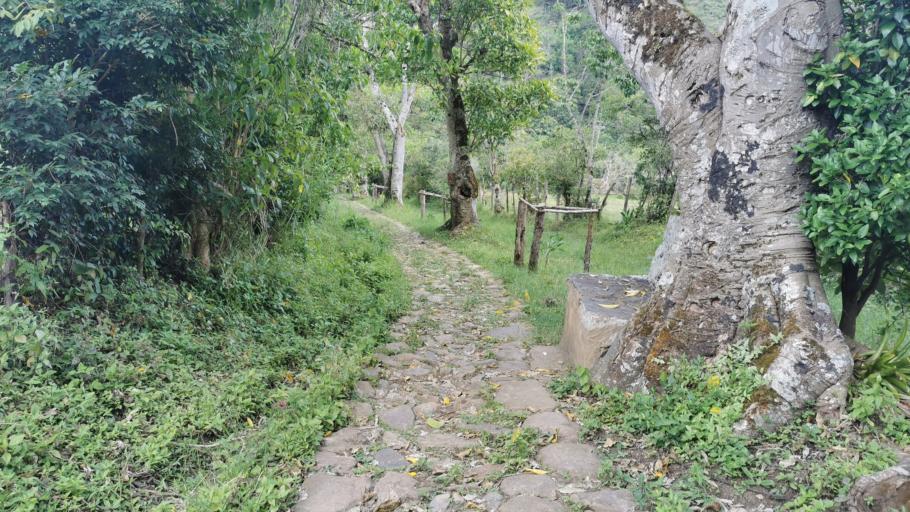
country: CO
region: Cundinamarca
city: Tenza
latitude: 5.0784
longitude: -73.4193
